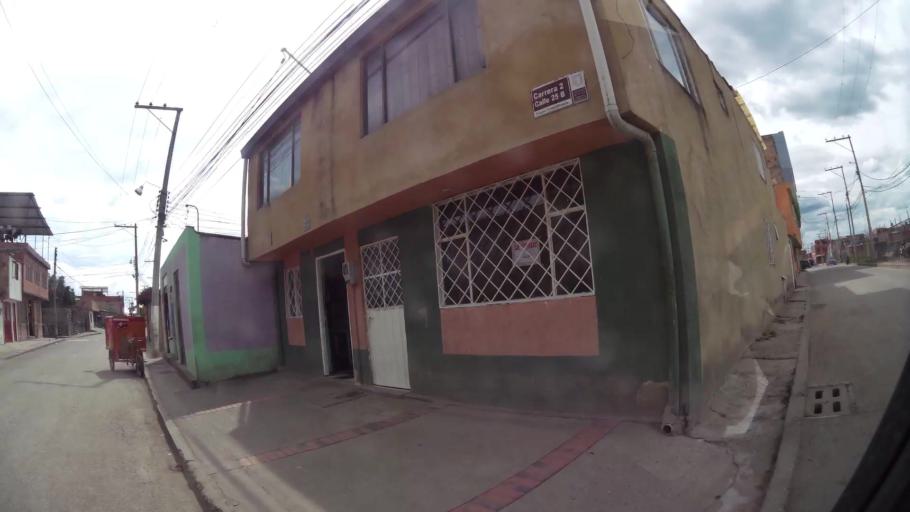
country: CO
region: Cundinamarca
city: Funza
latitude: 4.7086
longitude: -74.1957
